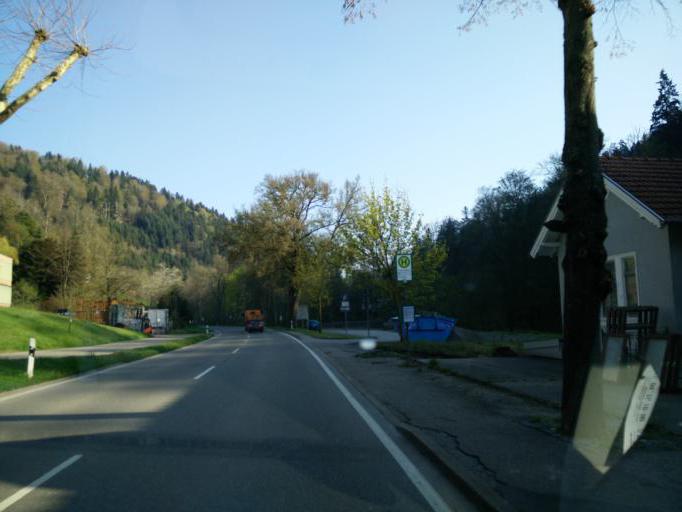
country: DE
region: Baden-Wuerttemberg
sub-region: Karlsruhe Region
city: Bad Liebenzell
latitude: 48.7617
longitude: 8.7295
